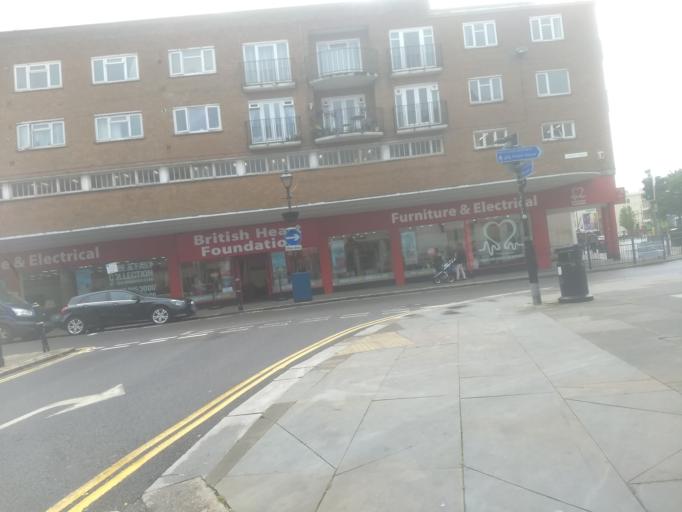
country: GB
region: England
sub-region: Kent
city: Dover
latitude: 51.1254
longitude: 1.3137
